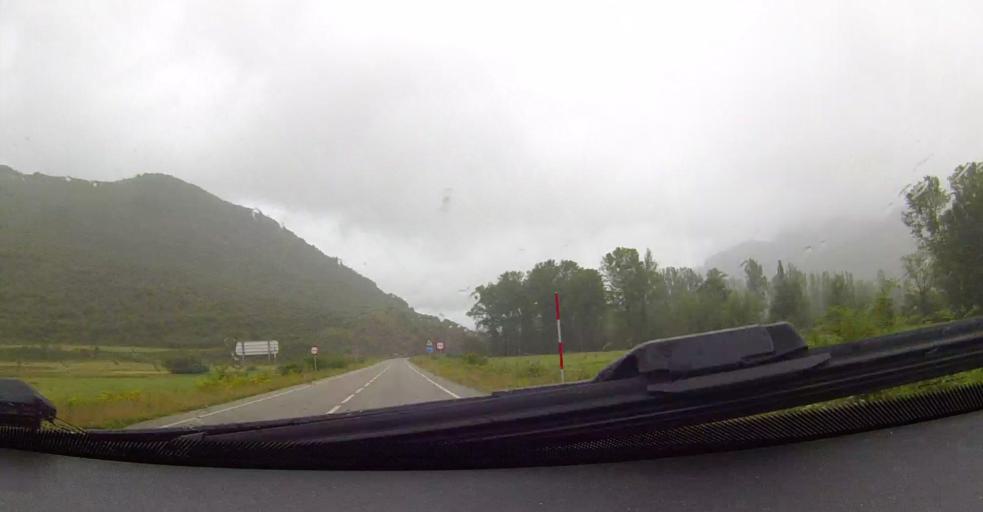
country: ES
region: Castille and Leon
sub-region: Provincia de Leon
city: Acebedo
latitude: 43.0433
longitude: -5.1134
